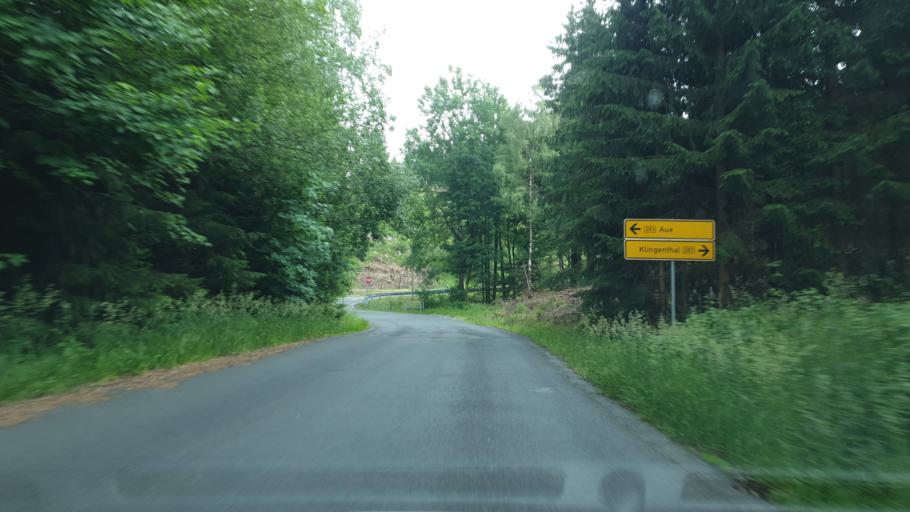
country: DE
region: Saxony
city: Tannenbergsthal
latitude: 50.4287
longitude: 12.4710
